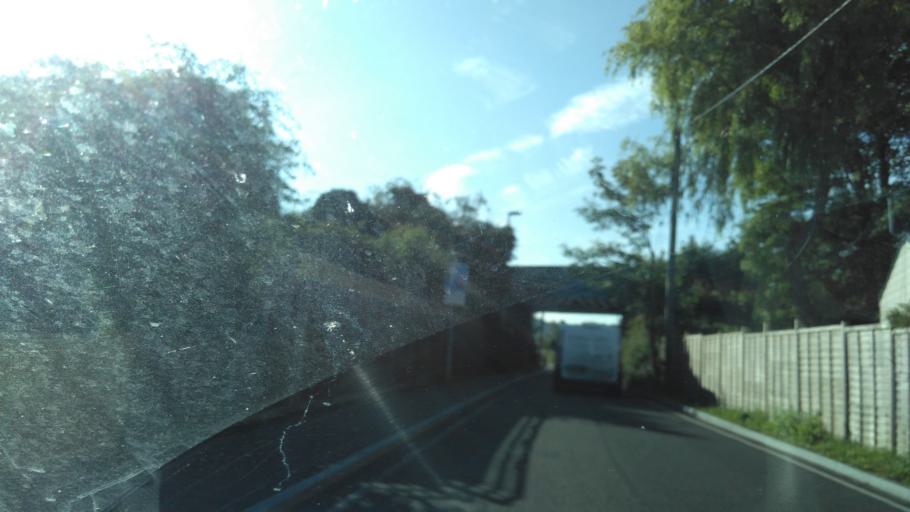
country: GB
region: England
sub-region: Kent
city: Whitstable
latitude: 51.3447
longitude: 0.9912
